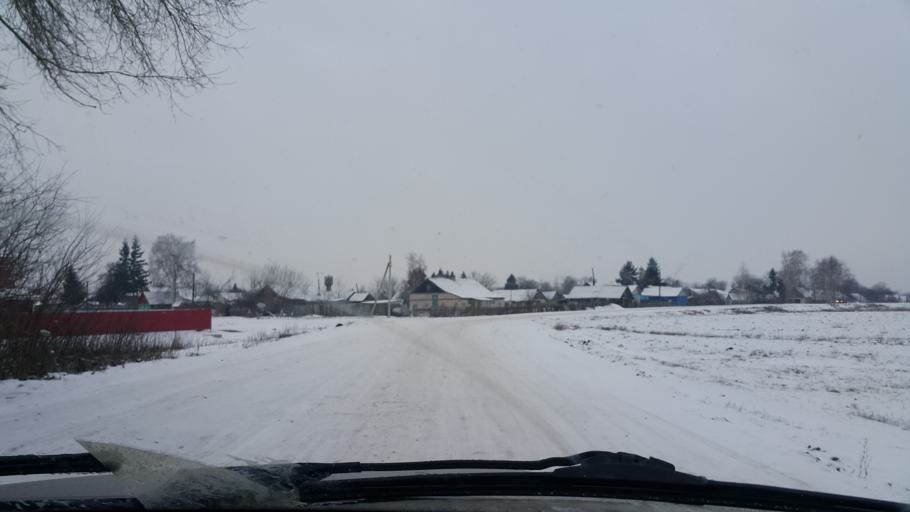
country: RU
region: Tambov
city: Inzhavino
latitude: 52.4692
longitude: 42.3903
